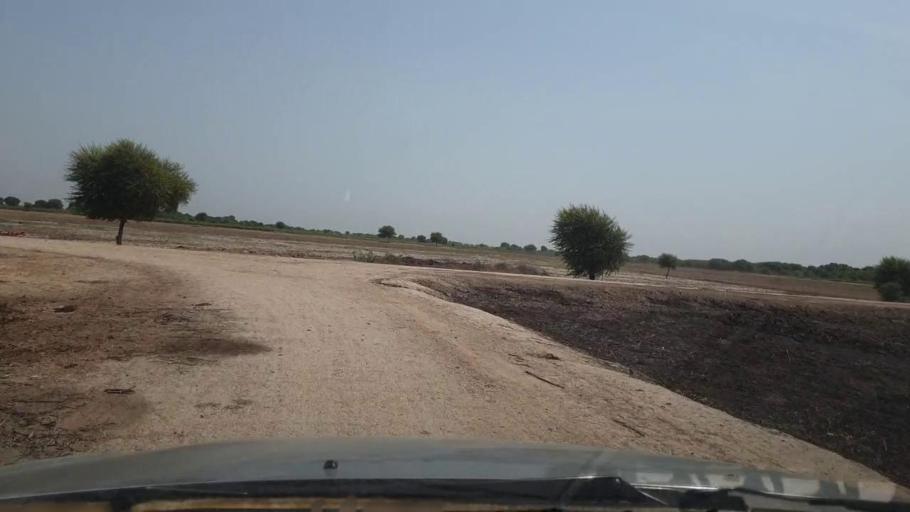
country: PK
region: Sindh
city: Chambar
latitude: 25.2572
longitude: 68.7572
